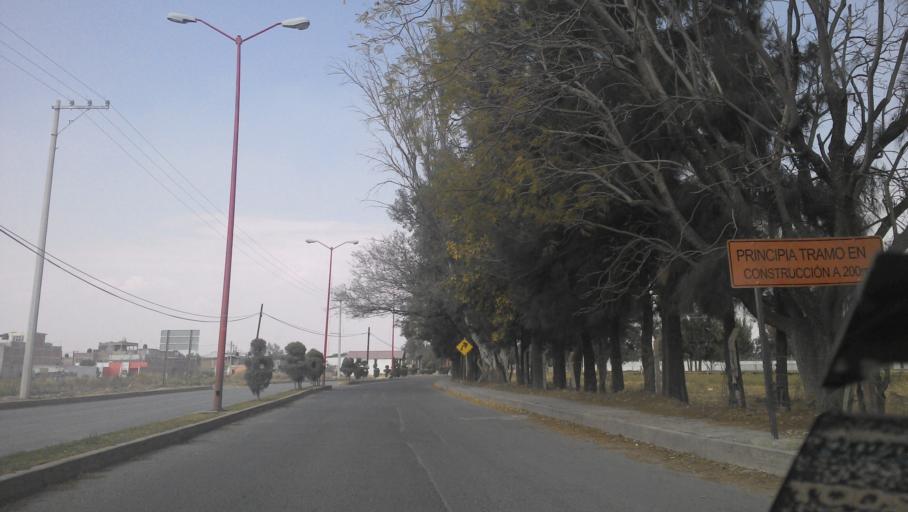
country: MX
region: Guanajuato
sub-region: San Francisco del Rincon
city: Fraccionamiento Villa Jardin
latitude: 20.9979
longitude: -101.8530
